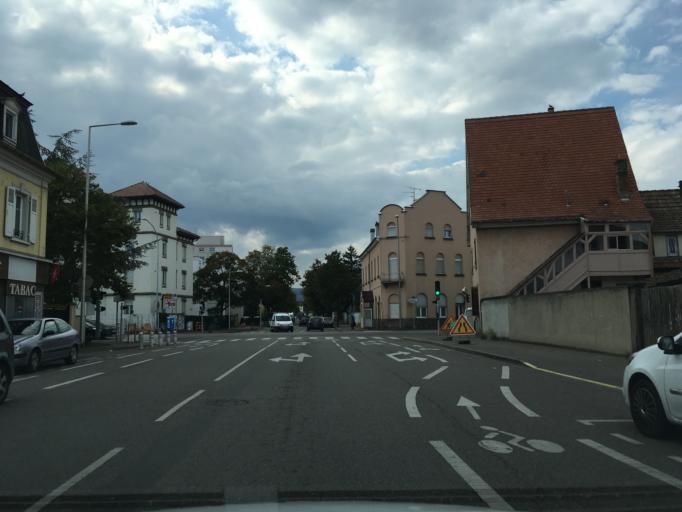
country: FR
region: Alsace
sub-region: Departement du Haut-Rhin
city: Colmar
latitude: 48.0852
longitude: 7.3581
